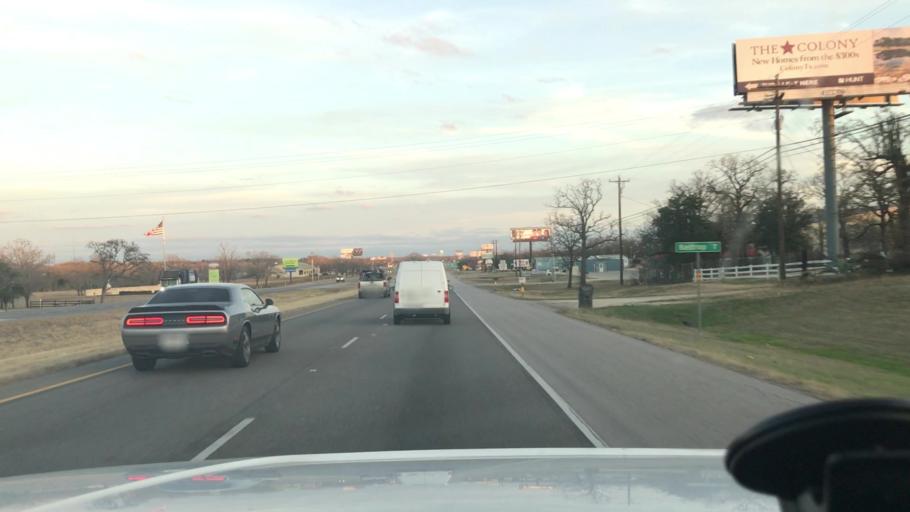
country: US
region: Texas
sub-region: Bastrop County
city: Wyldwood
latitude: 30.1208
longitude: -97.4305
